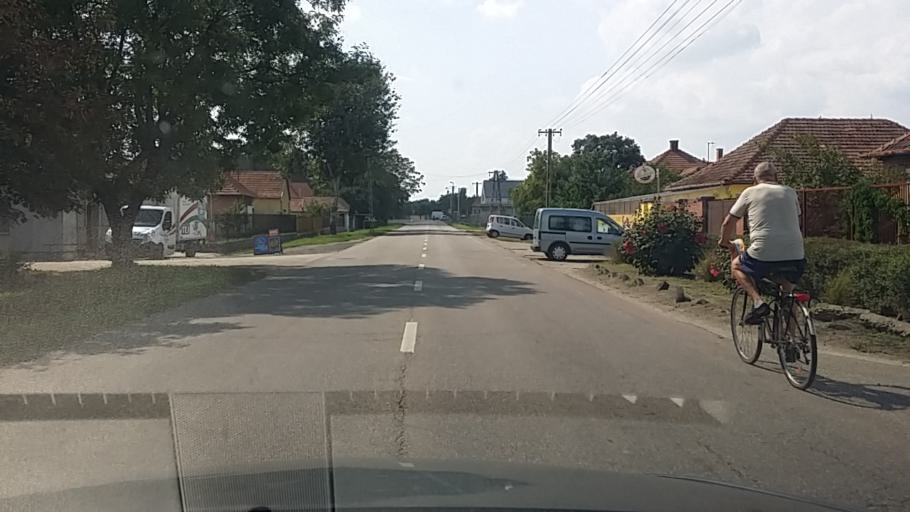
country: HU
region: Bacs-Kiskun
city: Kecskemet
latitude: 46.8963
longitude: 19.7298
